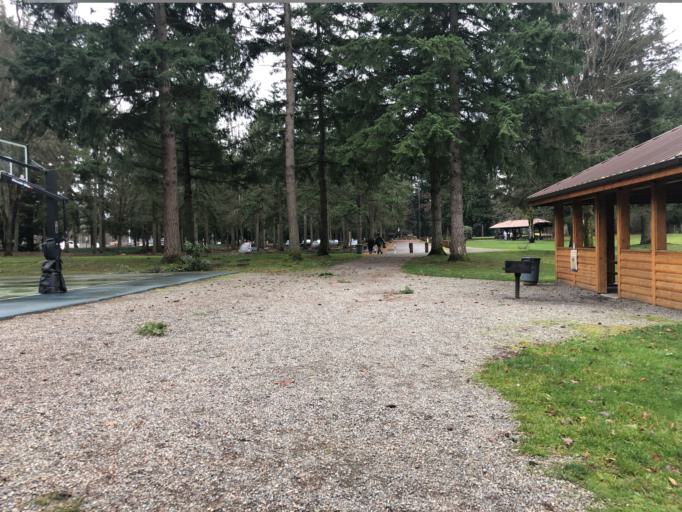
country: US
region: Washington
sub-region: King County
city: Lakeland South
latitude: 47.2742
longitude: -122.2806
